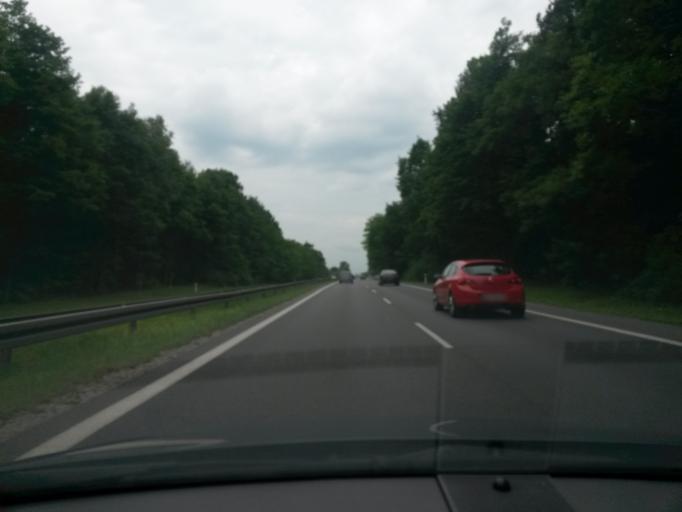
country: PL
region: Lodz Voivodeship
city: Zabia Wola
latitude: 52.0584
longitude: 20.7326
